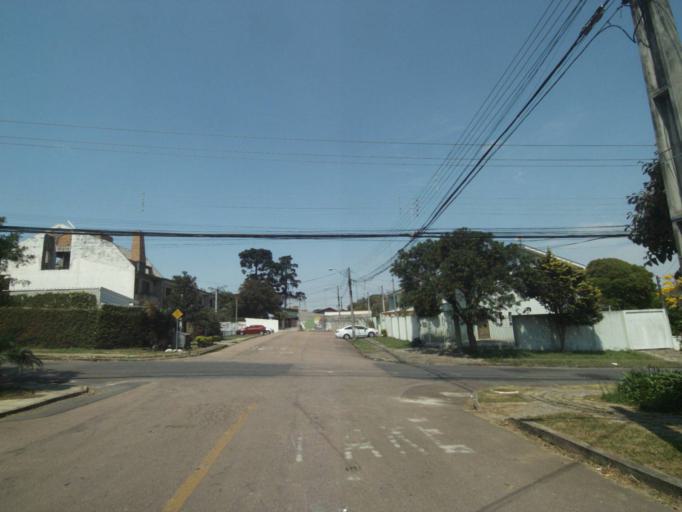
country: BR
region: Parana
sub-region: Curitiba
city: Curitiba
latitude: -25.4782
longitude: -49.3158
